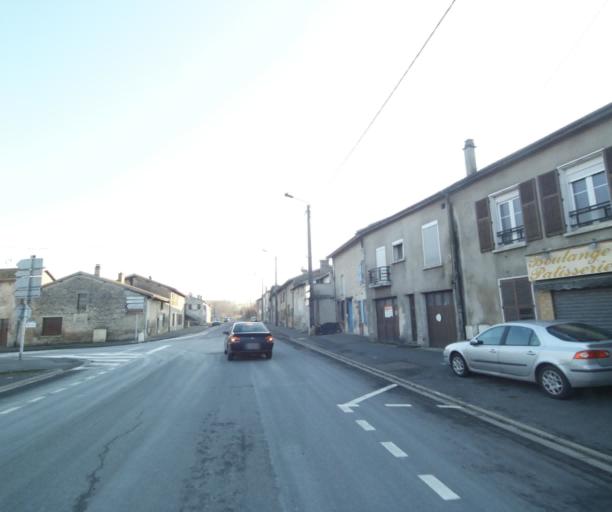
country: FR
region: Champagne-Ardenne
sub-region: Departement de la Haute-Marne
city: Chevillon
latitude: 48.5238
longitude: 5.1036
